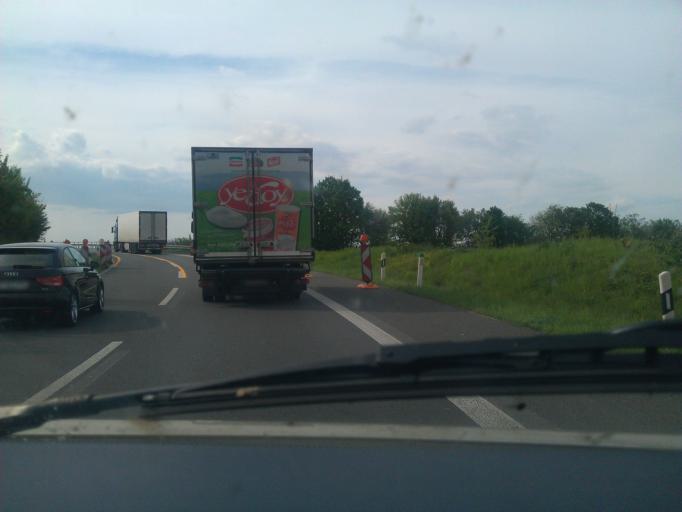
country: DE
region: North Rhine-Westphalia
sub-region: Regierungsbezirk Dusseldorf
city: Juchen
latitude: 51.1039
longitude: 6.4290
